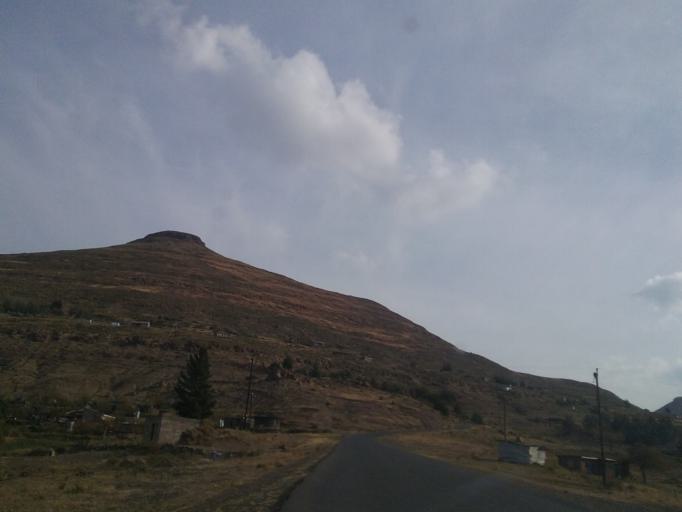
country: LS
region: Quthing
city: Quthing
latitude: -30.1936
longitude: 28.1187
